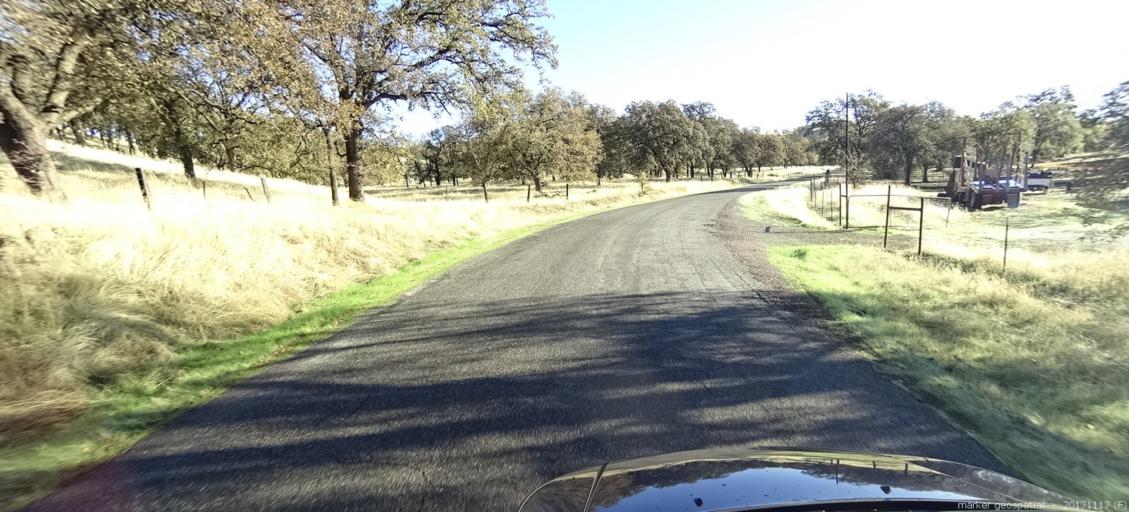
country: US
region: California
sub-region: Shasta County
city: Cottonwood
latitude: 40.4022
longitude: -122.1507
